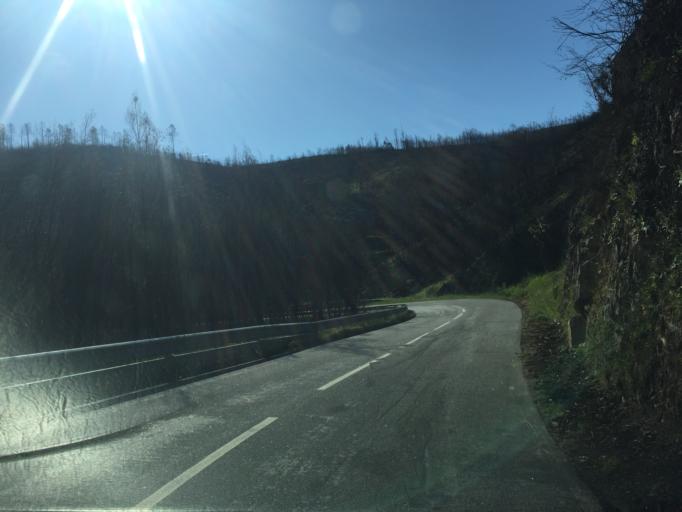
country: PT
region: Coimbra
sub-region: Pampilhosa da Serra
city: Pampilhosa da Serra
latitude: 40.0367
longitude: -7.9238
